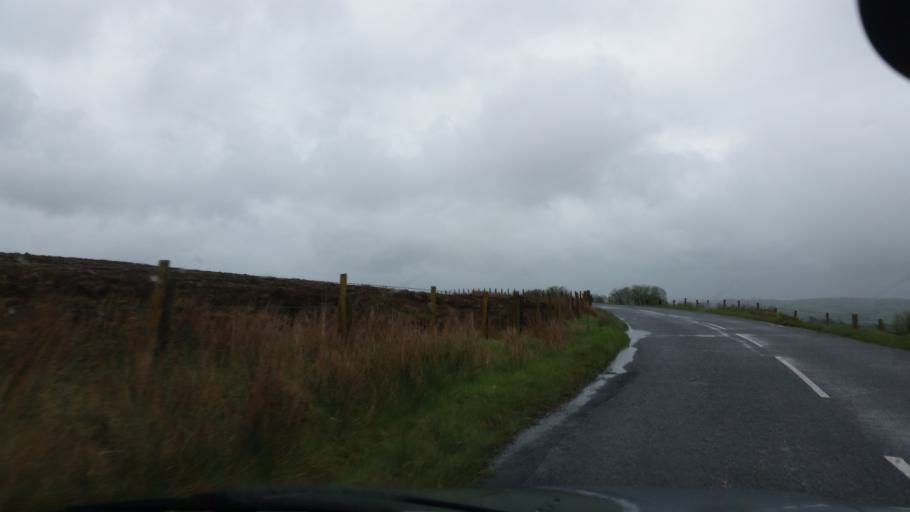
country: GB
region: Northern Ireland
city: Fintona
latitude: 54.4493
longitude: -7.3223
